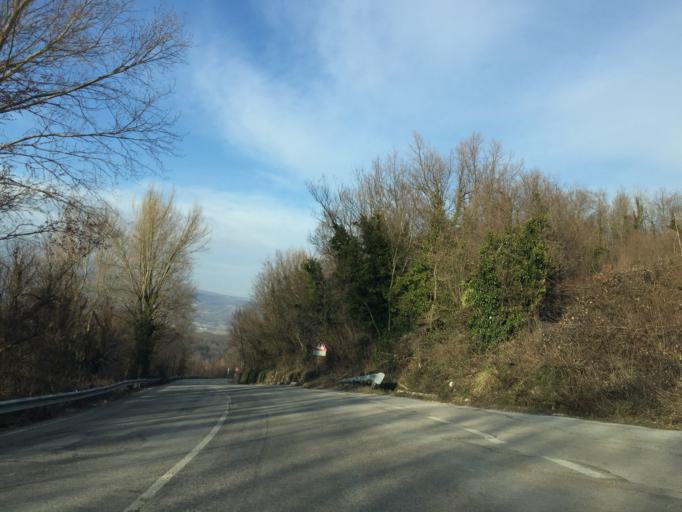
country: IT
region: Molise
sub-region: Provincia di Campobasso
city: San Massimo
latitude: 41.4881
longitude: 14.4060
